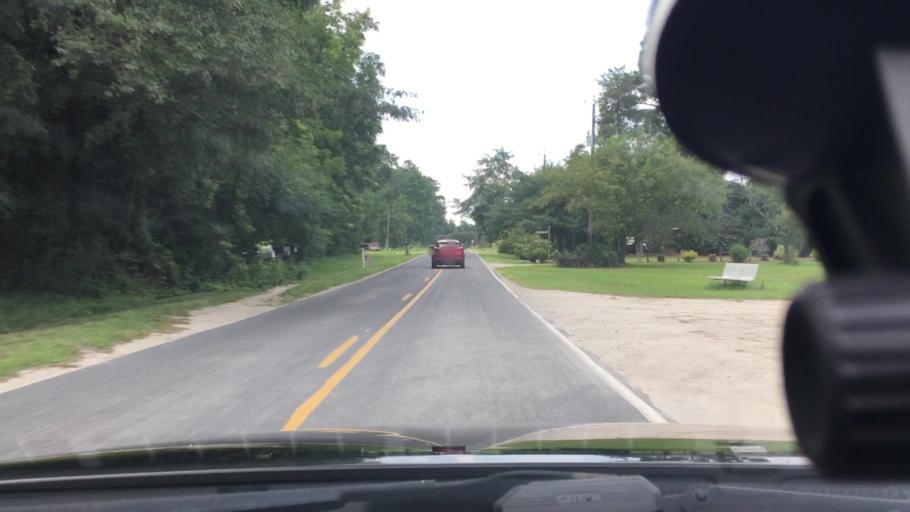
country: US
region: North Carolina
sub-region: Craven County
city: New Bern
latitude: 35.1755
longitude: -77.0528
